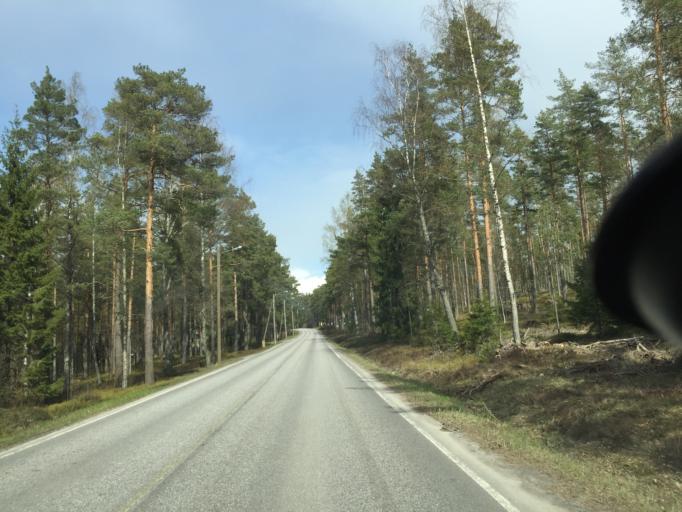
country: FI
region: Varsinais-Suomi
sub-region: Salo
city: Saerkisalo
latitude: 59.9780
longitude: 23.0096
